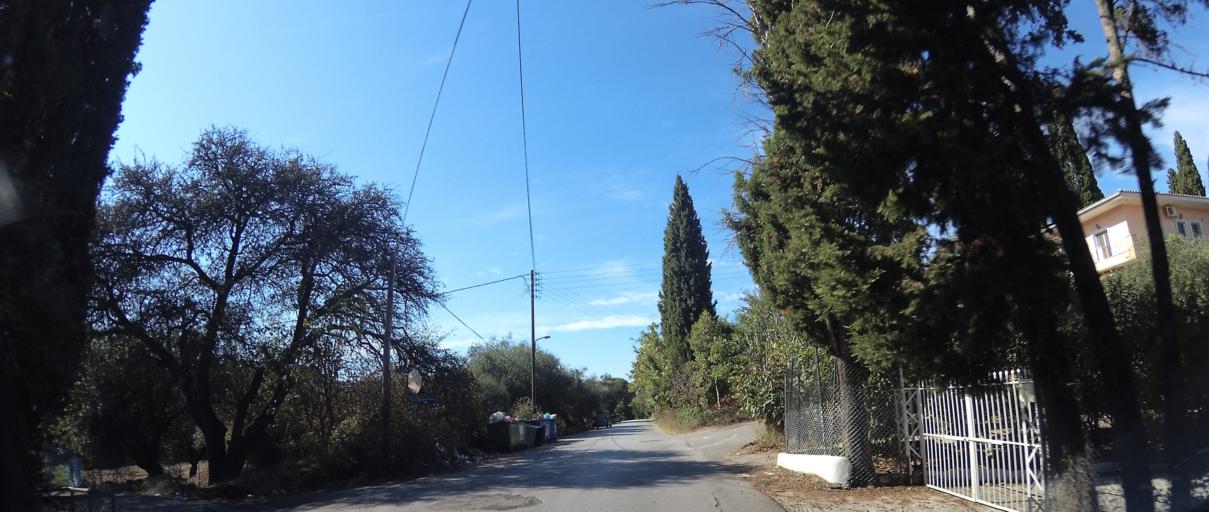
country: GR
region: Ionian Islands
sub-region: Nomos Kerkyras
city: Kontokali
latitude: 39.6375
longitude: 19.8586
